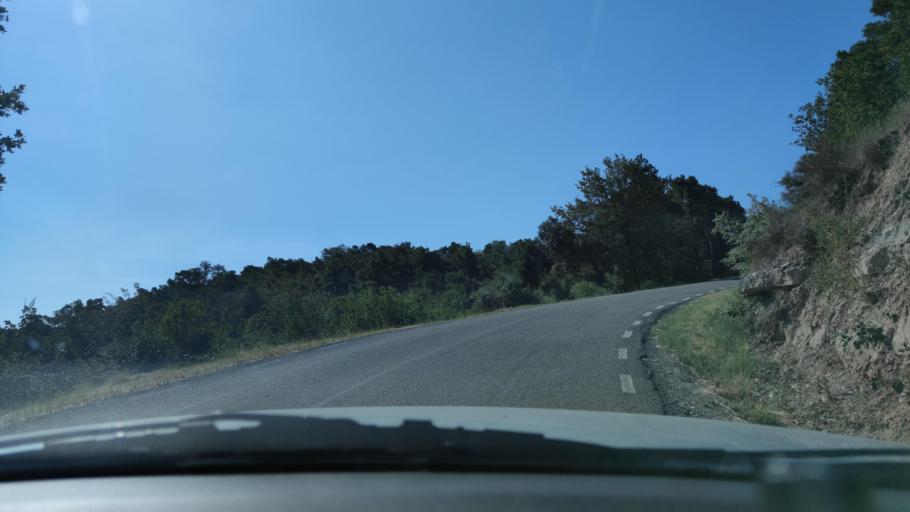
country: ES
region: Catalonia
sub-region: Provincia de Barcelona
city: Pujalt
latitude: 41.7080
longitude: 1.3804
